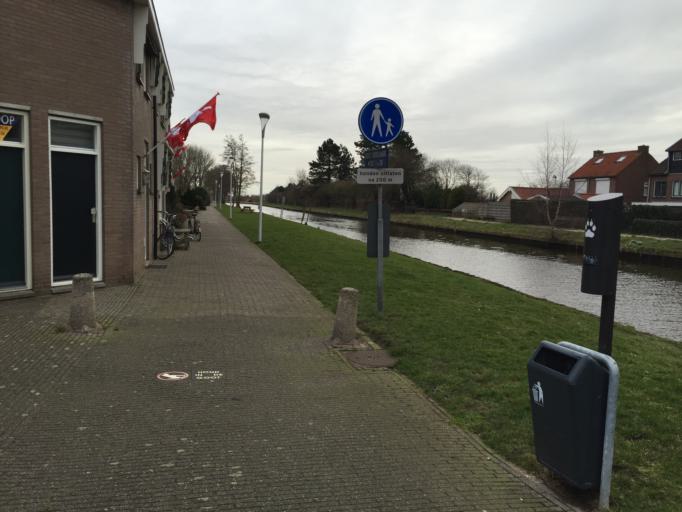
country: NL
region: Utrecht
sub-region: Gemeente Oudewater
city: Oudewater
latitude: 52.0203
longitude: 4.8724
